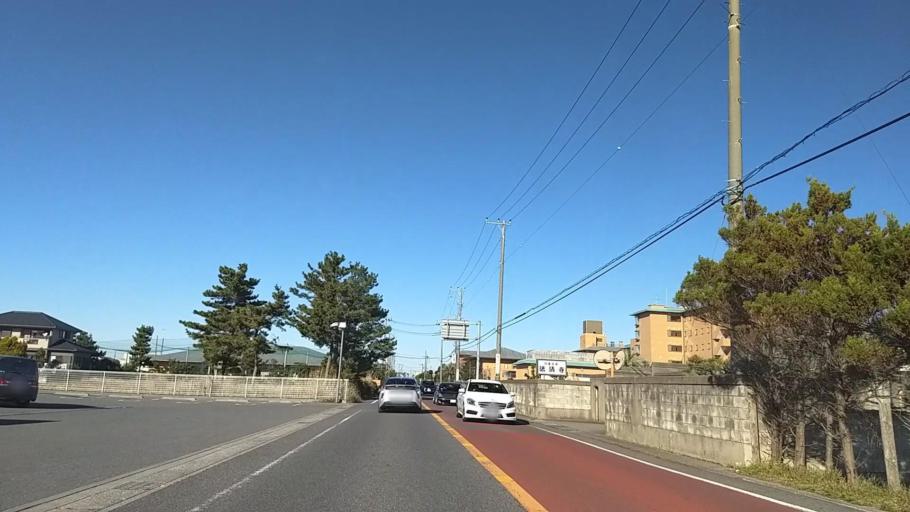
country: JP
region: Chiba
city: Mobara
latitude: 35.3735
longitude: 140.3876
